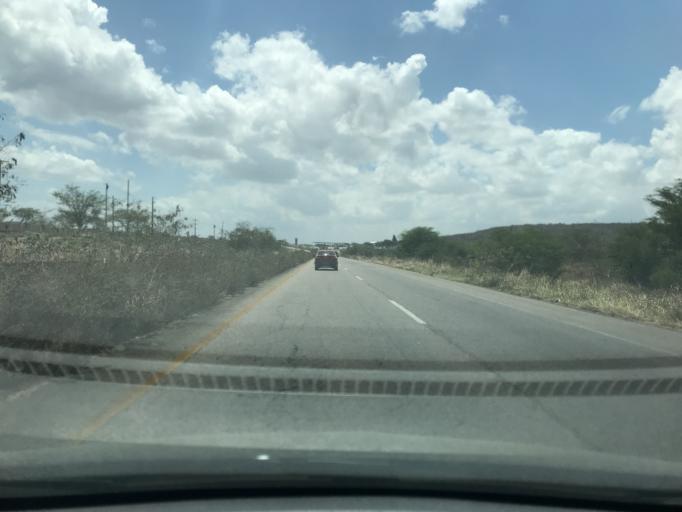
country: BR
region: Pernambuco
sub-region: Bezerros
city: Bezerros
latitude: -8.2953
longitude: -35.8760
